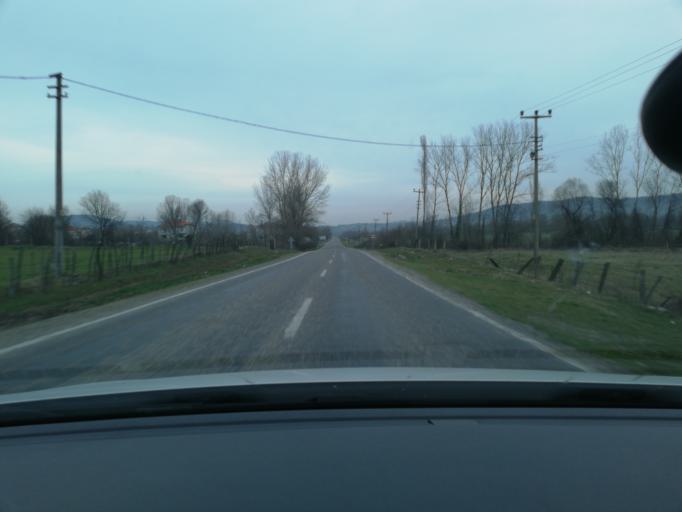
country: TR
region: Zonguldak
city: Saltukova
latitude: 41.5030
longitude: 32.0981
